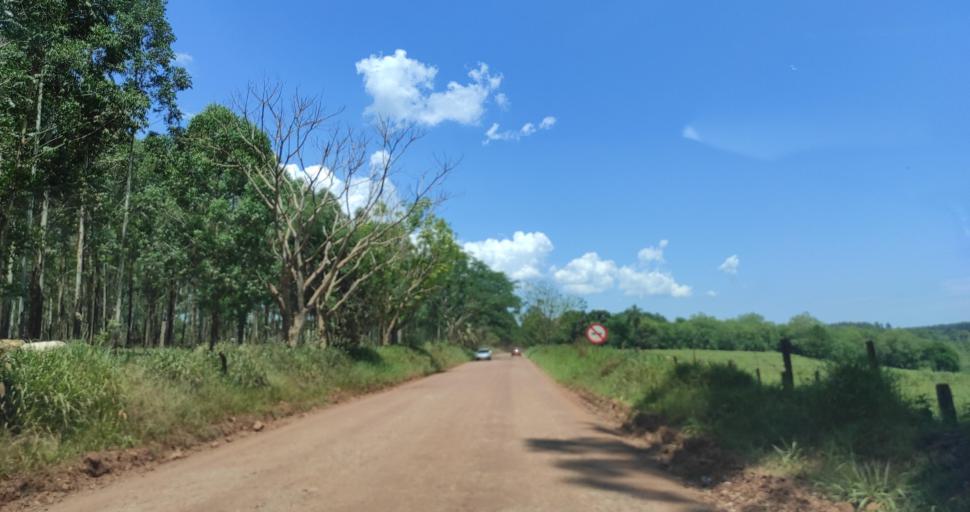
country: AR
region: Misiones
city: Ruiz de Montoya
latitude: -27.0421
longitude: -55.0256
